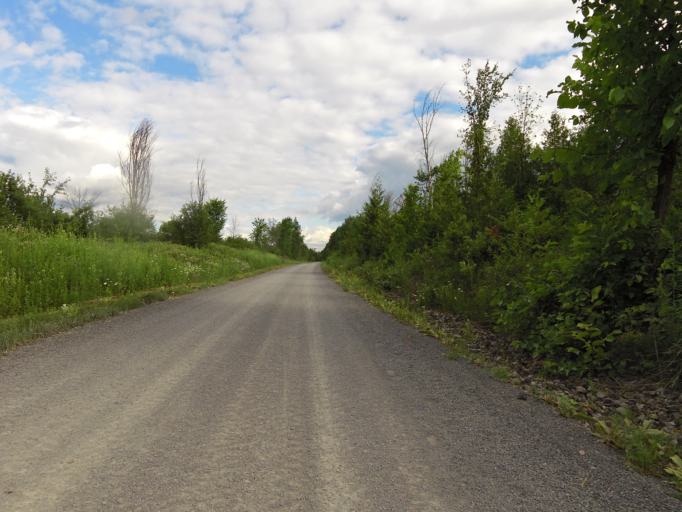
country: CA
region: Ontario
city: Arnprior
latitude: 45.2998
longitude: -76.2645
